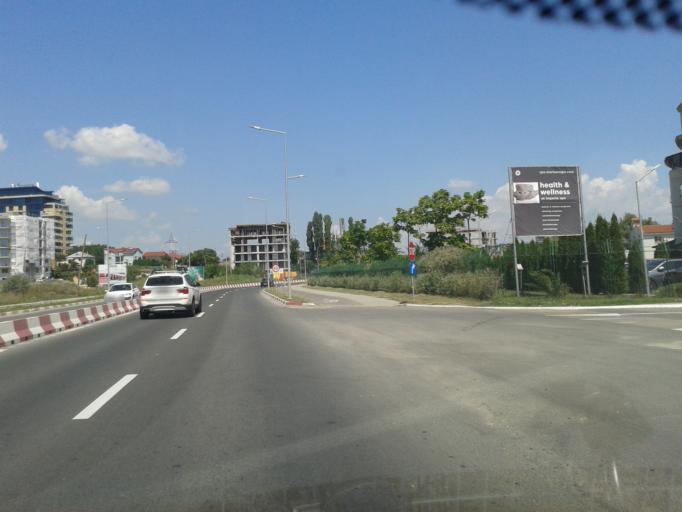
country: RO
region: Constanta
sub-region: Comuna Navodari
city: Navodari
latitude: 44.2857
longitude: 28.6171
